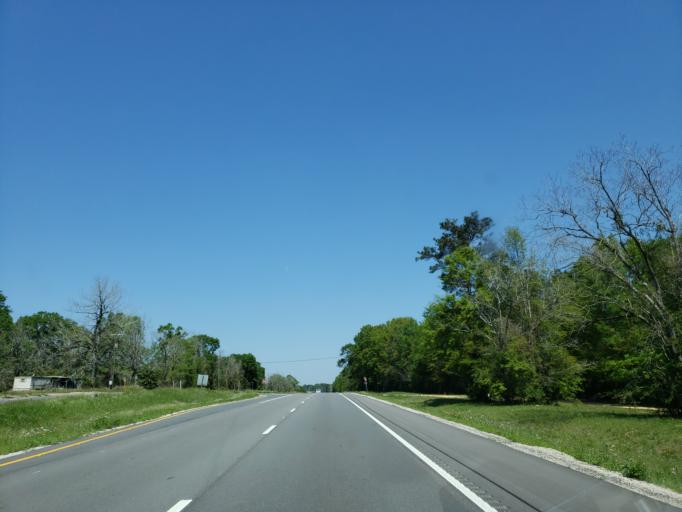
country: US
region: Mississippi
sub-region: Stone County
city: Wiggins
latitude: 30.8964
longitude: -89.1669
